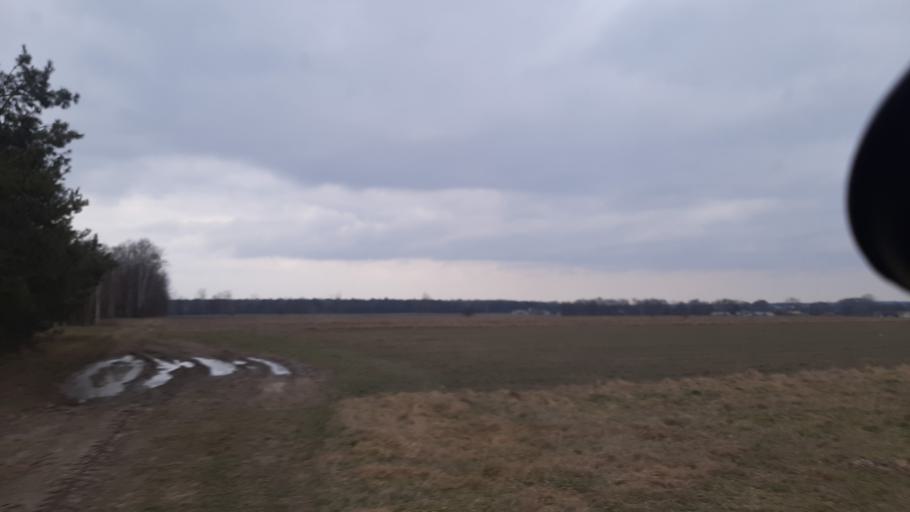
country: PL
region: Lublin Voivodeship
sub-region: Powiat lubelski
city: Garbow
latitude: 51.3847
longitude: 22.4070
